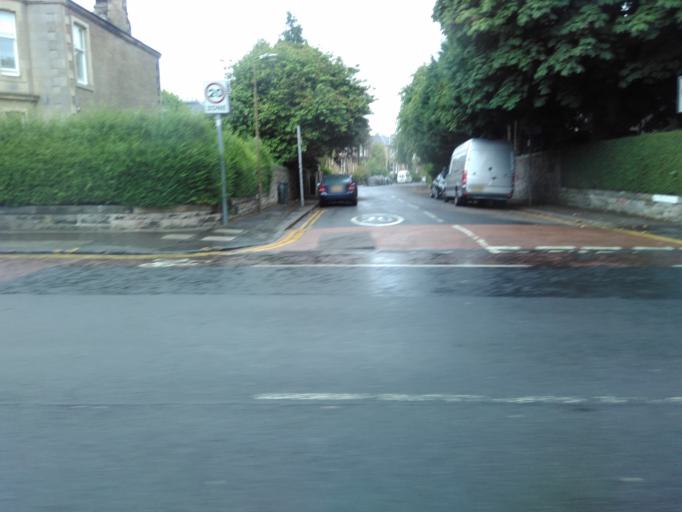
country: GB
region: Scotland
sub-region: Edinburgh
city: Edinburgh
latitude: 55.9305
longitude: -3.1709
